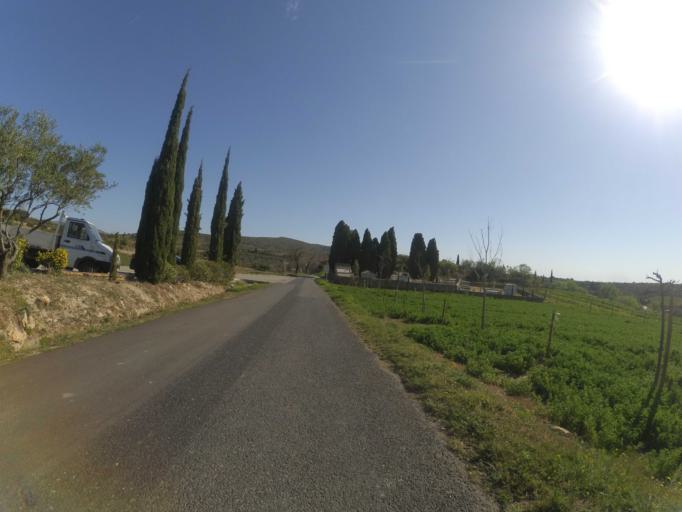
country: FR
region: Languedoc-Roussillon
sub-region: Departement des Pyrenees-Orientales
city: Estagel
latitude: 42.7576
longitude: 2.7499
